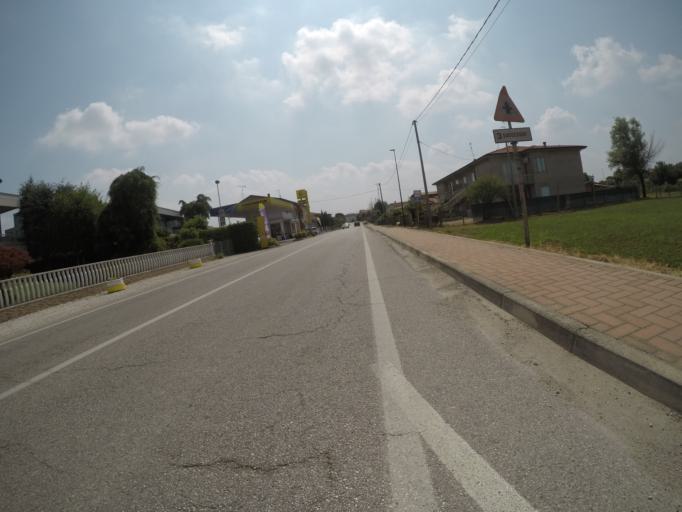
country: IT
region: Veneto
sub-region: Provincia di Rovigo
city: Villanova del Ghebbo Canton
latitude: 45.0594
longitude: 11.6379
